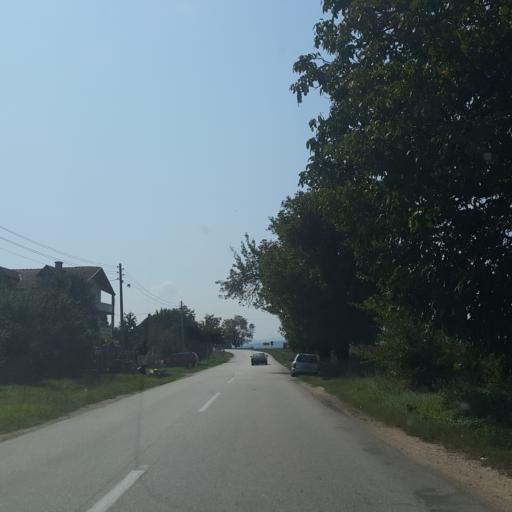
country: RS
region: Central Serbia
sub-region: Zajecarski Okrug
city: Knjazevac
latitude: 43.6793
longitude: 22.2903
